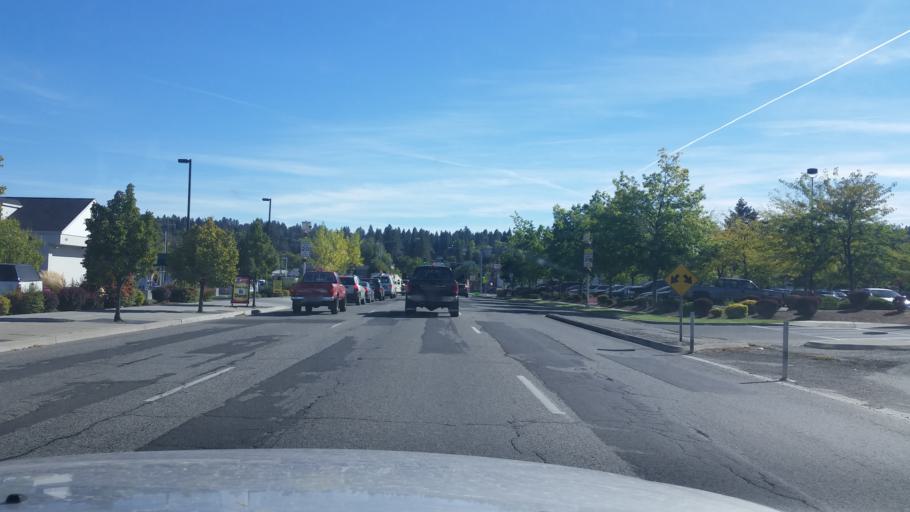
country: US
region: Washington
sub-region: Spokane County
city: Spokane
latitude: 47.6530
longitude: -117.3604
